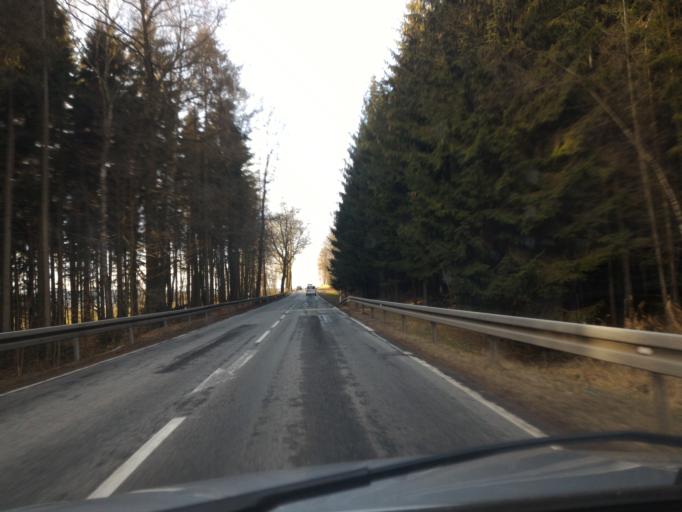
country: DE
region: Saxony
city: Crostau
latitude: 51.0554
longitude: 14.4585
